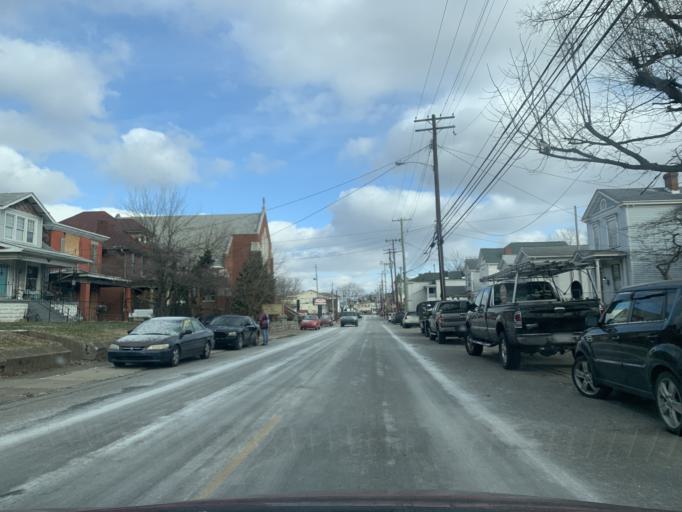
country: US
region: Kentucky
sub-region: Jefferson County
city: Louisville
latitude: 38.2683
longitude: -85.7916
